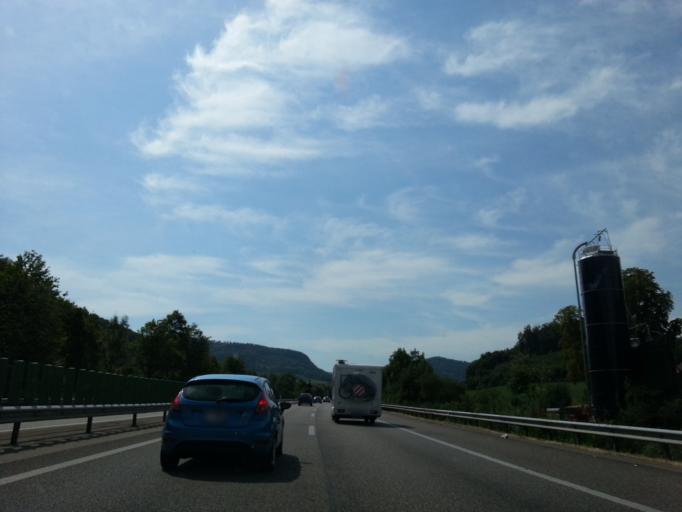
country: CH
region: Basel-Landschaft
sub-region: Bezirk Sissach
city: Tenniken
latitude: 47.4267
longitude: 7.8092
